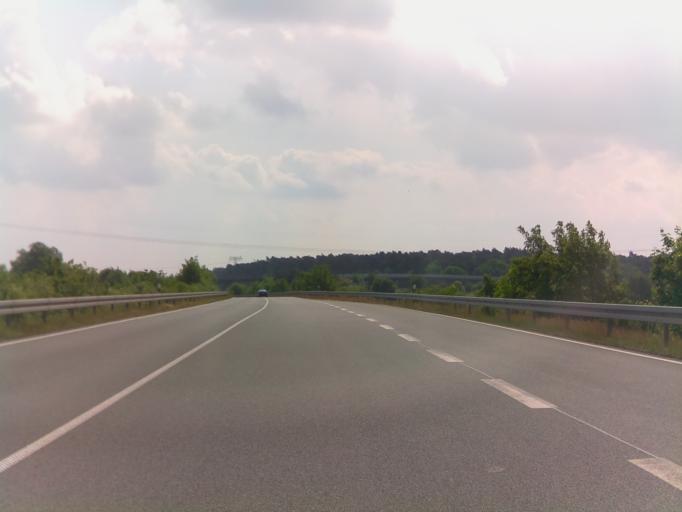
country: DE
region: Saxony-Anhalt
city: Stendal
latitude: 52.5747
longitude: 11.8364
